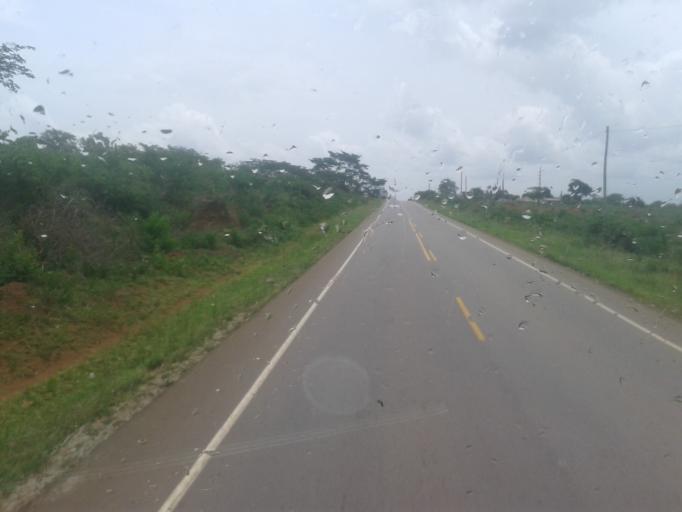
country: UG
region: Western Region
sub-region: Kiryandongo District
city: Masindi Port
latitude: 1.7556
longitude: 32.0213
